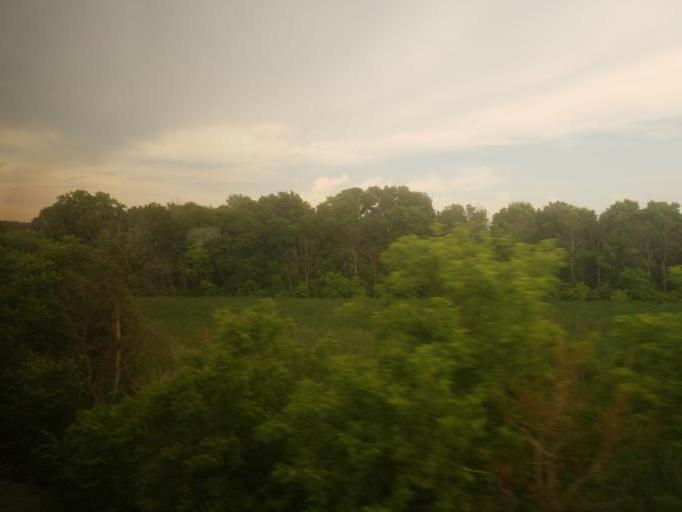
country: US
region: Illinois
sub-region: Bureau County
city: Princeton
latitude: 41.3895
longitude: -89.5137
